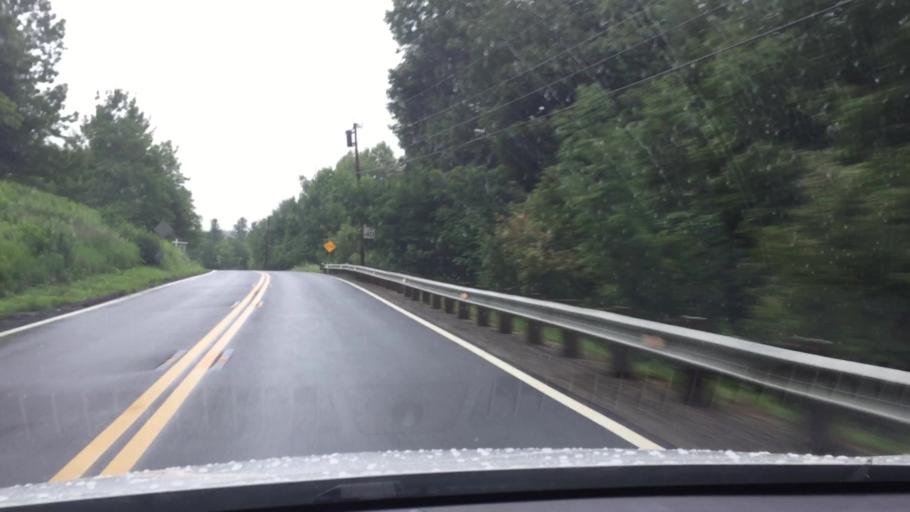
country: US
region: Massachusetts
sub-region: Berkshire County
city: Becket
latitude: 42.3480
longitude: -73.1203
